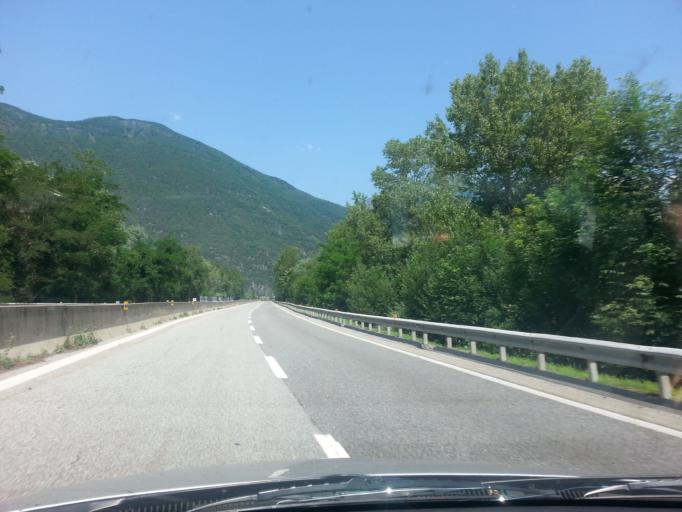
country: IT
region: Piedmont
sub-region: Provincia Verbano-Cusio-Ossola
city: Pallanzeno
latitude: 46.0339
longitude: 8.2749
